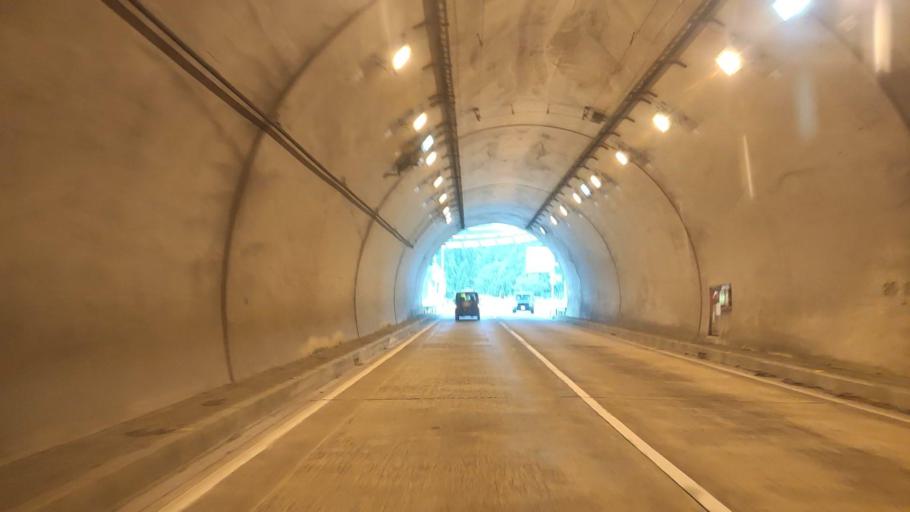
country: JP
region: Fukui
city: Takefu
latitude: 35.8229
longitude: 136.1037
